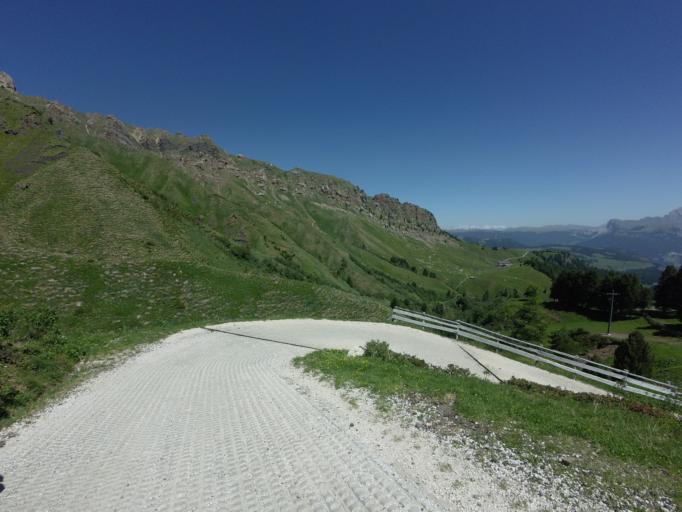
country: IT
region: Trentino-Alto Adige
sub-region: Provincia di Trento
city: Mazzin
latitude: 46.4999
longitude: 11.6497
